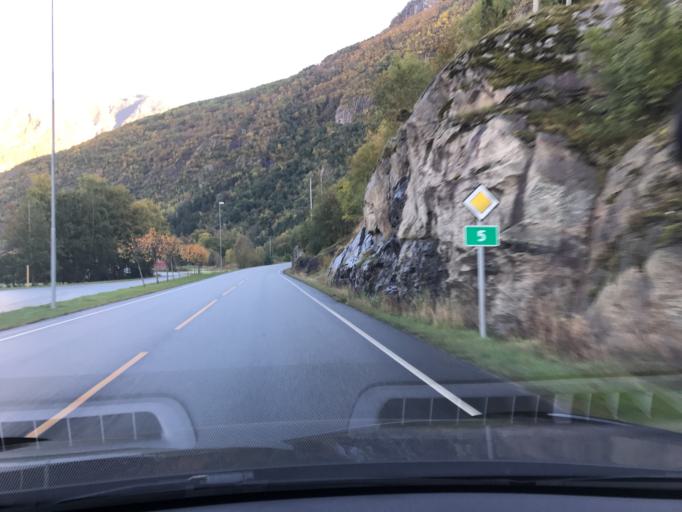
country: NO
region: Sogn og Fjordane
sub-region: Laerdal
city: Laerdalsoyri
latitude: 61.0976
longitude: 7.4741
